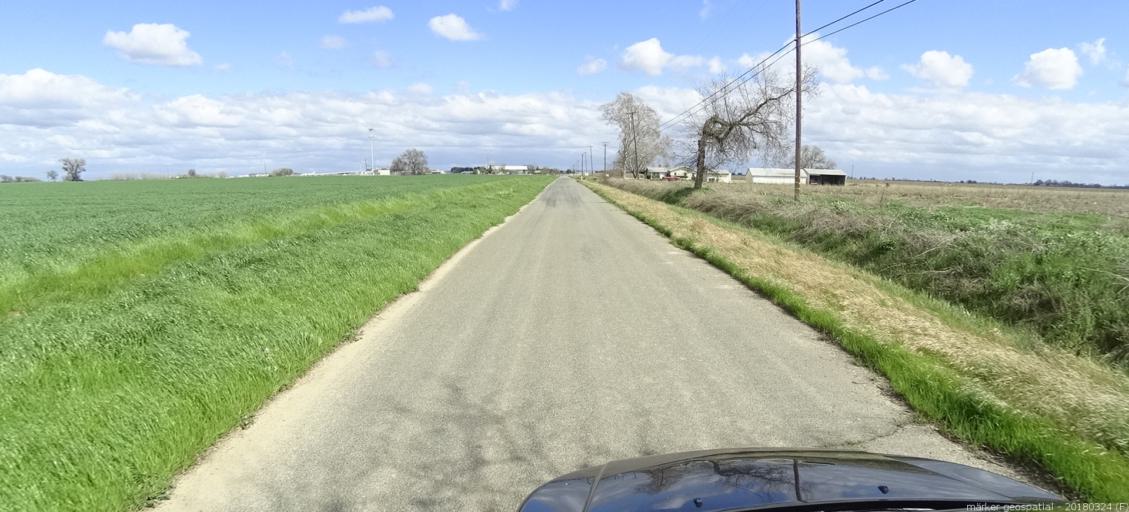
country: US
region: California
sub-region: Yolo County
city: West Sacramento
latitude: 38.6854
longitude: -121.6176
